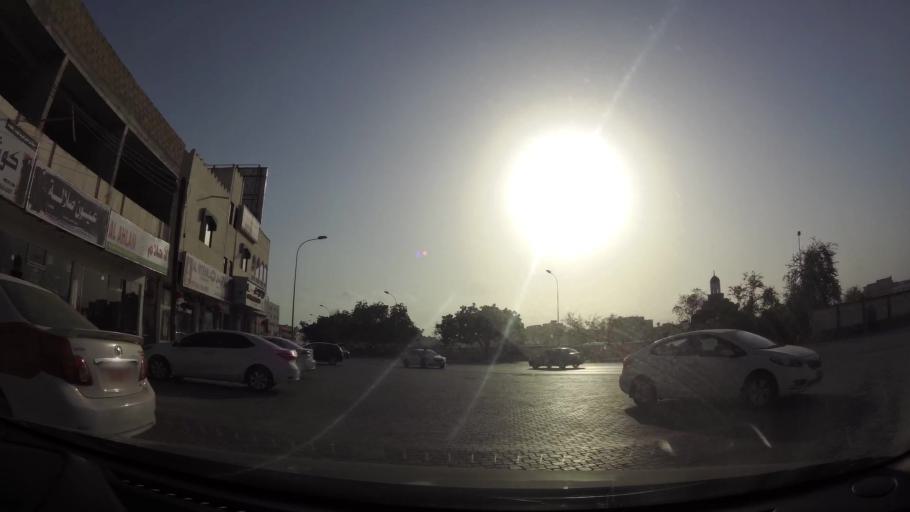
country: OM
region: Zufar
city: Salalah
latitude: 17.0116
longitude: 54.0903
